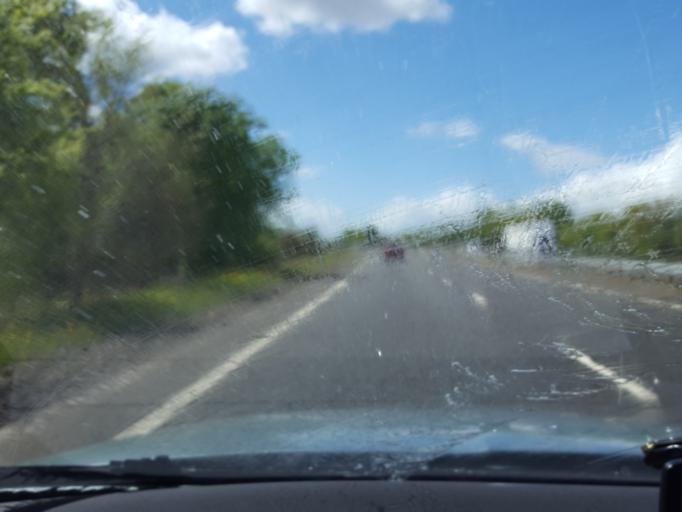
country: GB
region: Scotland
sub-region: Angus
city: Letham
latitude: 56.7135
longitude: -2.7961
